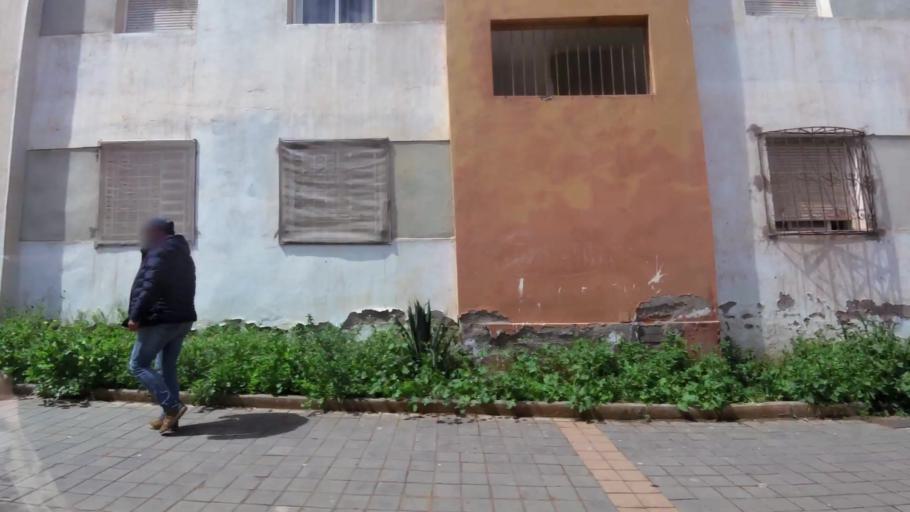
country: MA
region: Grand Casablanca
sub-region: Nouaceur
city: Dar Bouazza
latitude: 33.5364
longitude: -7.7170
